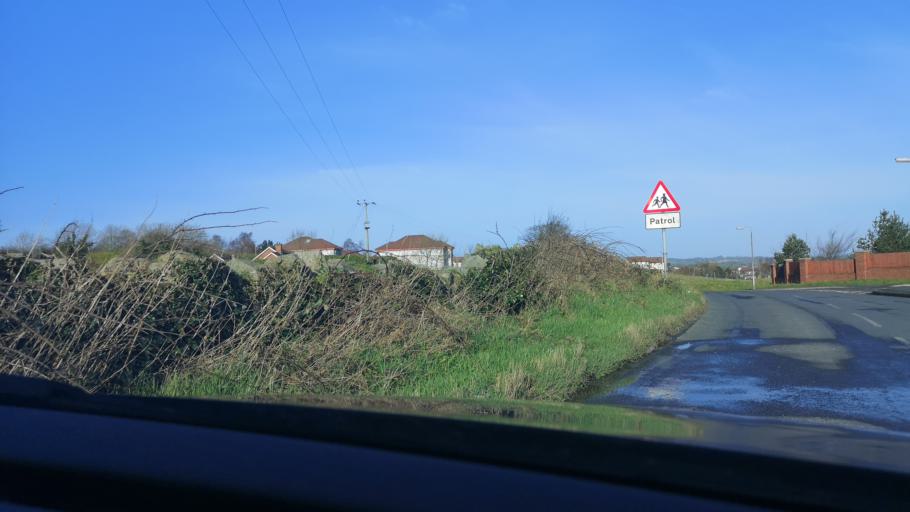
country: GB
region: Northern Ireland
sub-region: Newry and Mourne District
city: Newry
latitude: 54.1738
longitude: -6.3532
